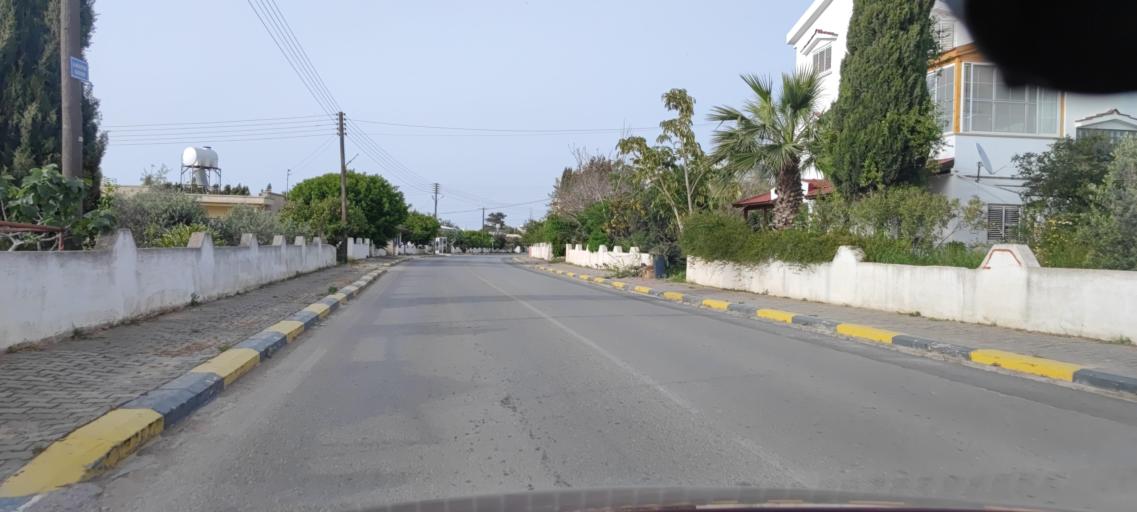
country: CY
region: Ammochostos
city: Leonarisso
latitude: 35.5301
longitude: 34.1852
